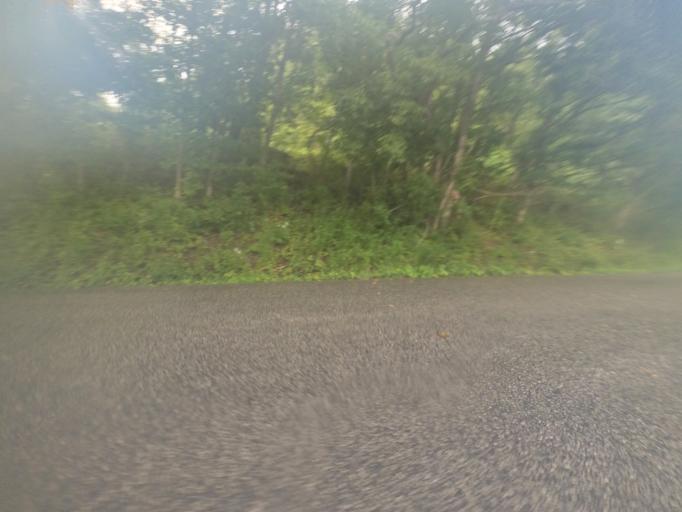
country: US
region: West Virginia
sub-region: Cabell County
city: Huntington
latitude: 38.3778
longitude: -82.4002
